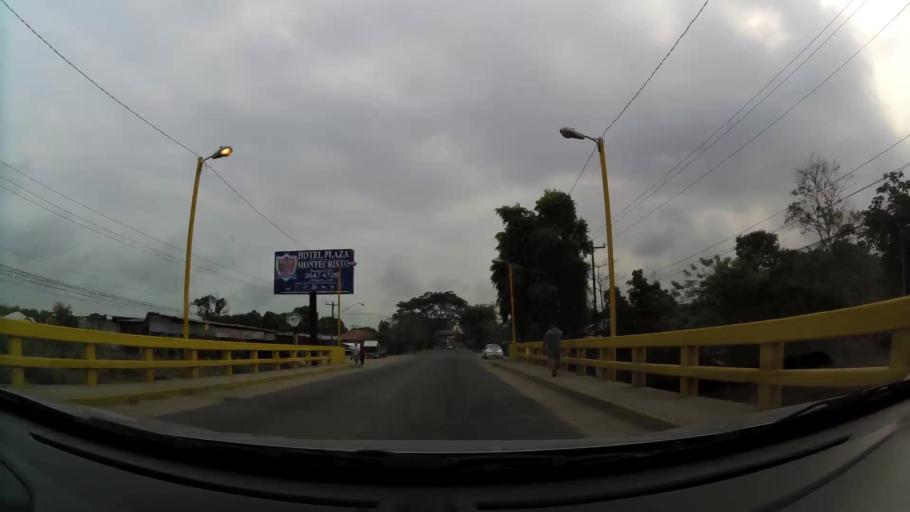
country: HN
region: Yoro
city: El Progreso
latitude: 15.4258
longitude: -87.7981
